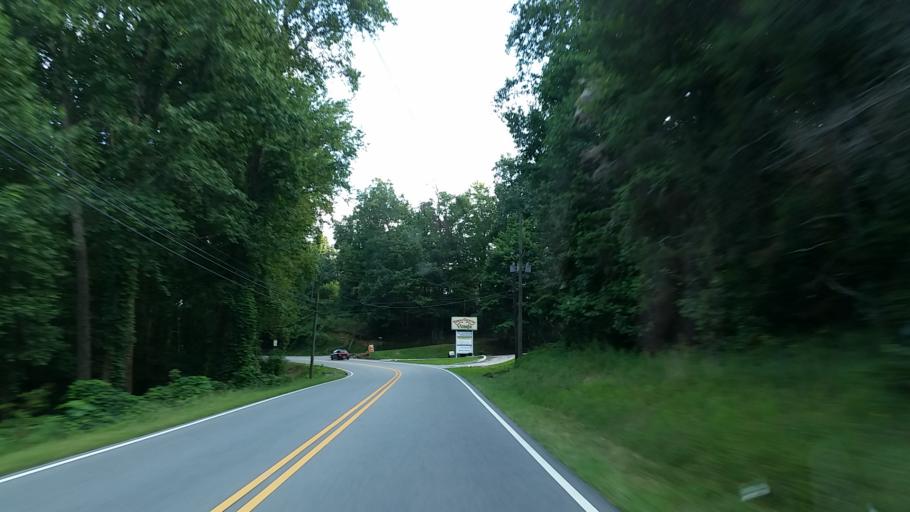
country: US
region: Georgia
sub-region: Lumpkin County
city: Dahlonega
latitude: 34.5451
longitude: -83.9928
